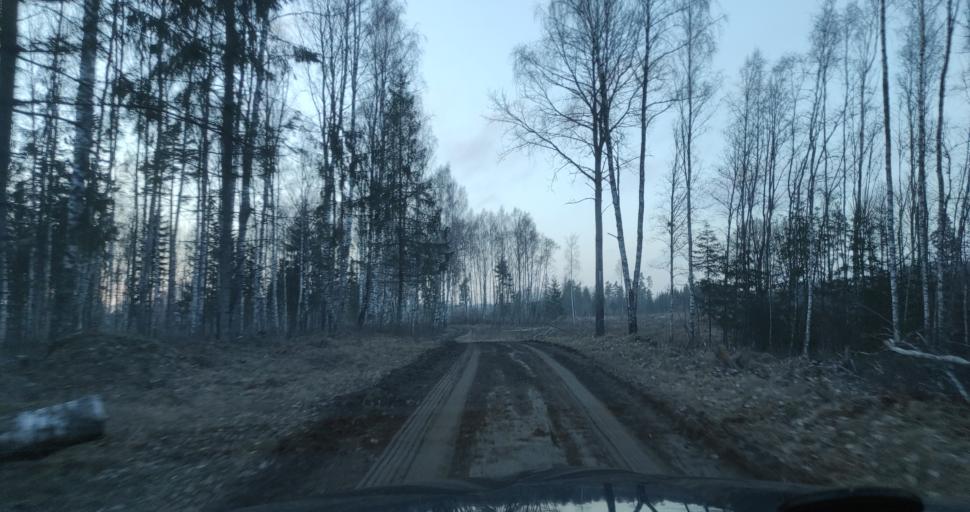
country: LV
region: Kuldigas Rajons
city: Kuldiga
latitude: 56.8107
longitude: 21.8274
